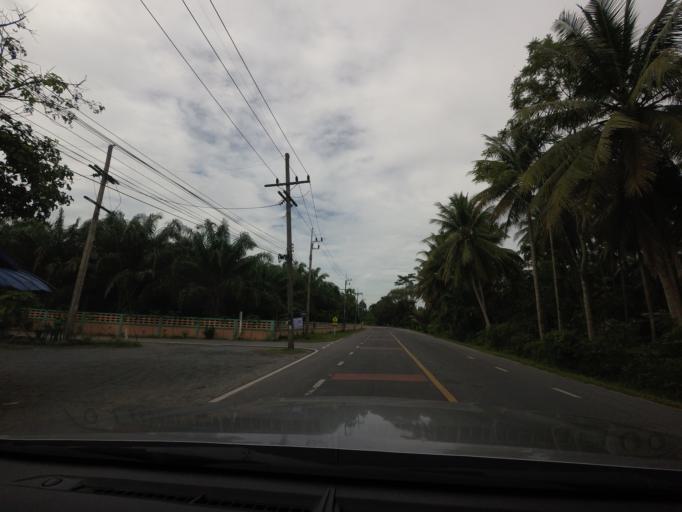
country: TH
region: Nakhon Si Thammarat
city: Phra Phrom
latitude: 8.2883
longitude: 99.9452
